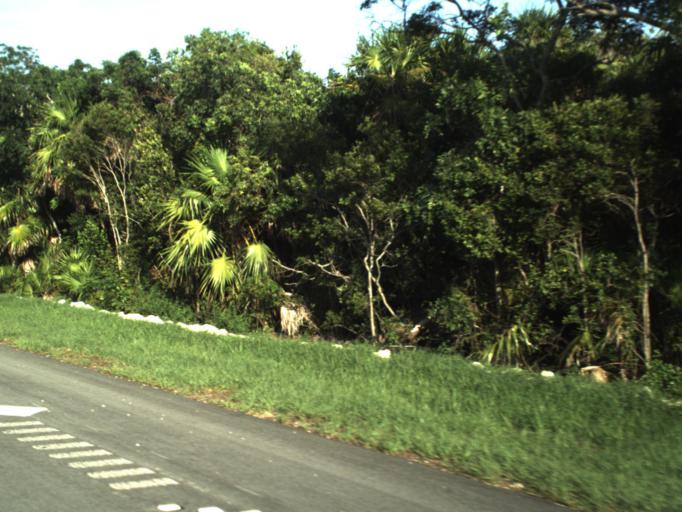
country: US
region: Florida
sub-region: Monroe County
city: Marathon
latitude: 24.7390
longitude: -81.0024
